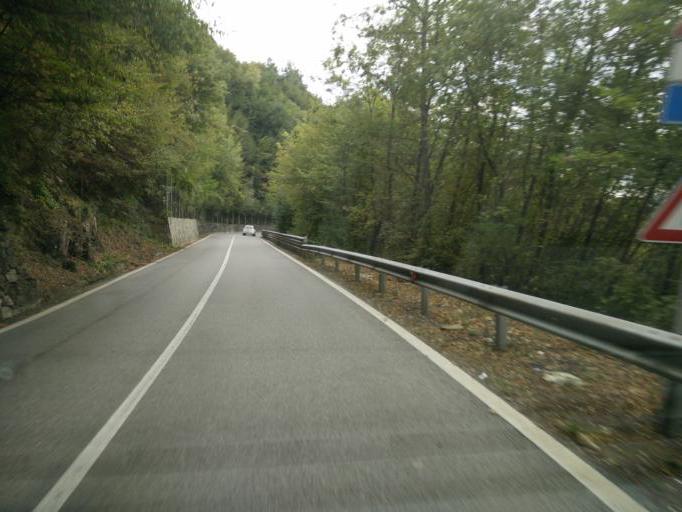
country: IT
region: Tuscany
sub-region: Provincia di Massa-Carrara
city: Fivizzano
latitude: 44.2218
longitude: 10.0996
